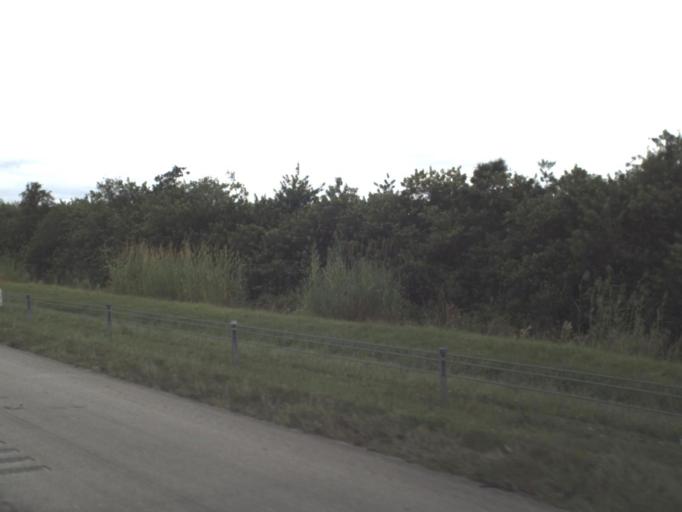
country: US
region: Florida
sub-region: Martin County
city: Hobe Sound
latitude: 27.0098
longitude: -80.2137
